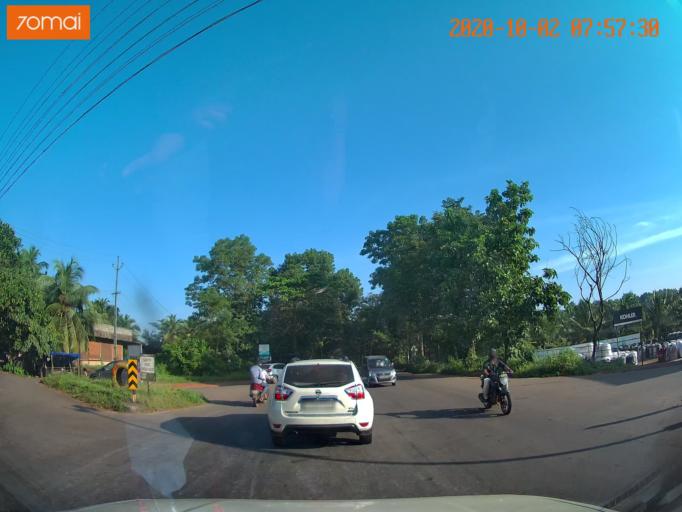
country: IN
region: Kerala
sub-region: Kozhikode
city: Ferokh
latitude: 11.2002
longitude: 75.8670
